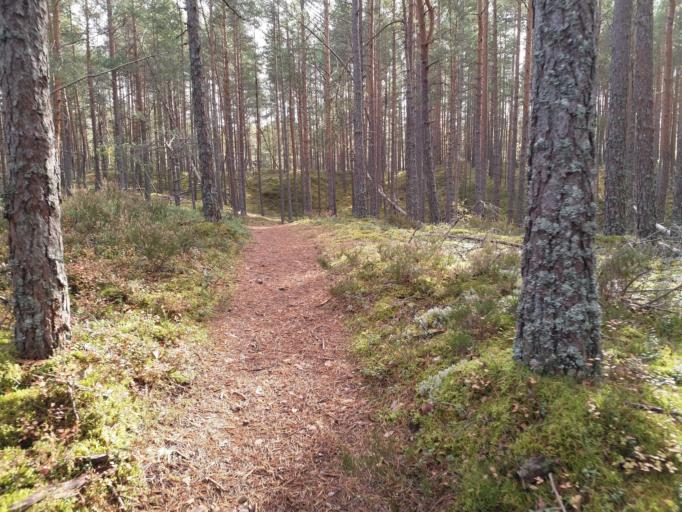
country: LV
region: Dundaga
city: Dundaga
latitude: 57.6512
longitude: 22.2589
